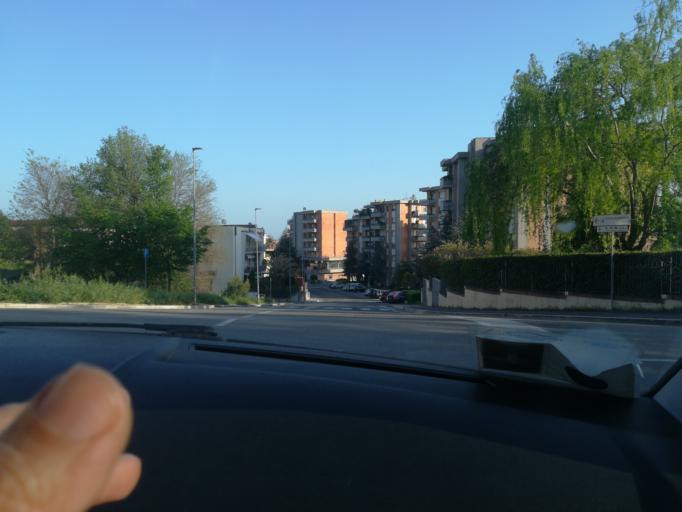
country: IT
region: The Marches
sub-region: Provincia di Macerata
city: Macerata
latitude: 43.2925
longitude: 13.4327
